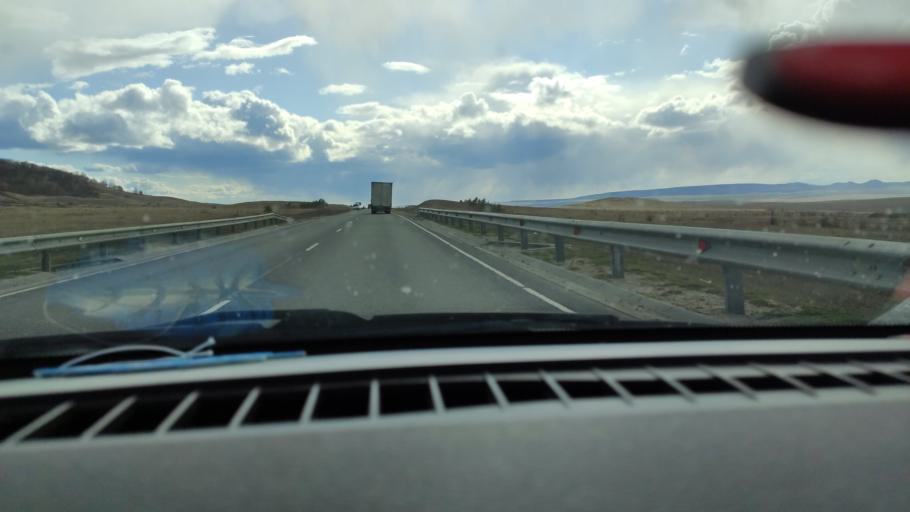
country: RU
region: Saratov
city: Alekseyevka
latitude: 52.3606
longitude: 47.9533
